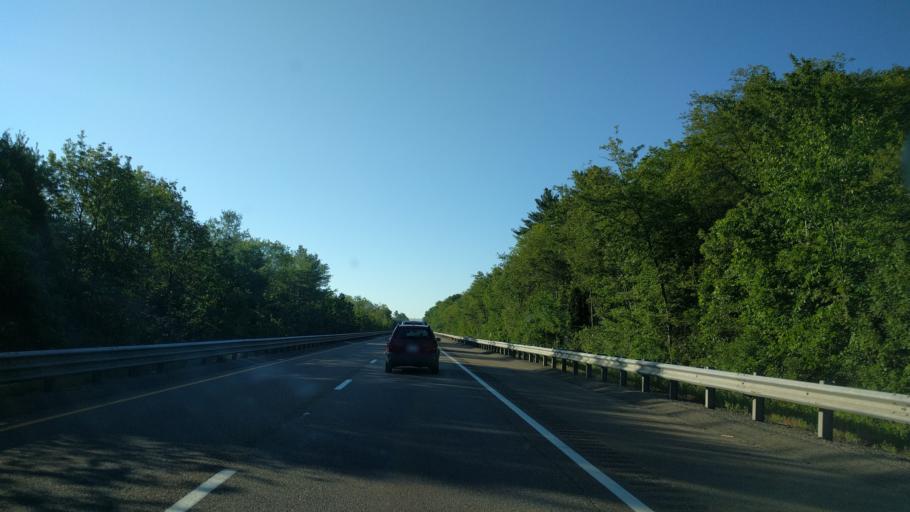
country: US
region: Massachusetts
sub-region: Bristol County
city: Raynham Center
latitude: 41.9219
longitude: -70.9947
